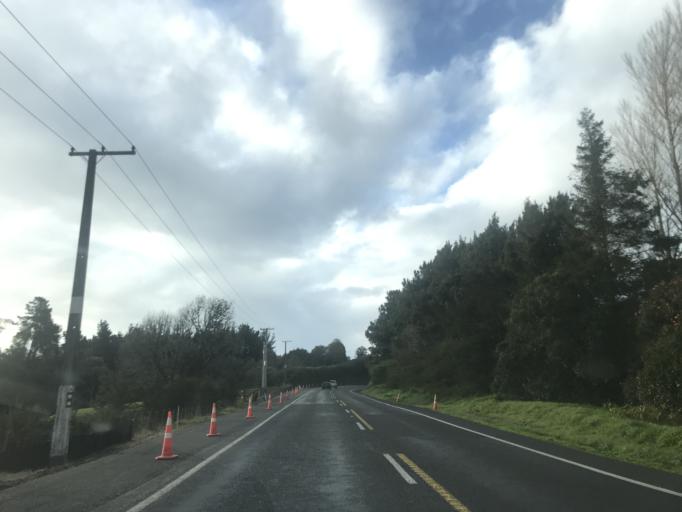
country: NZ
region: Bay of Plenty
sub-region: Western Bay of Plenty District
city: Katikati
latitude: -37.5304
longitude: 175.9146
